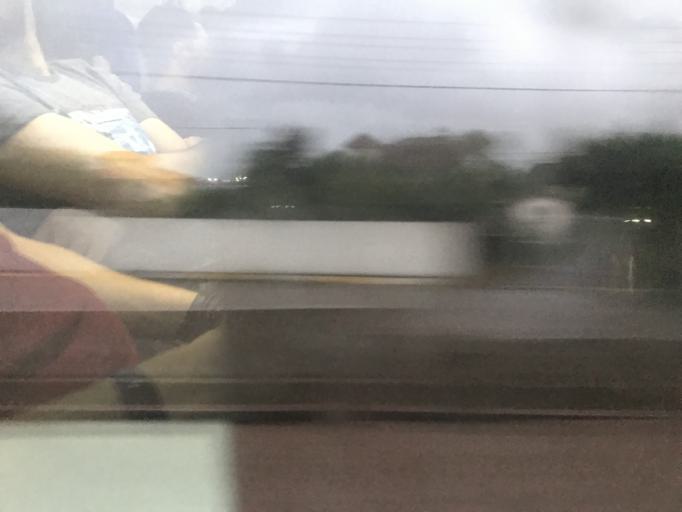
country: TR
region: Kocaeli
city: Ulasli
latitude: 40.7780
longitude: 29.6900
